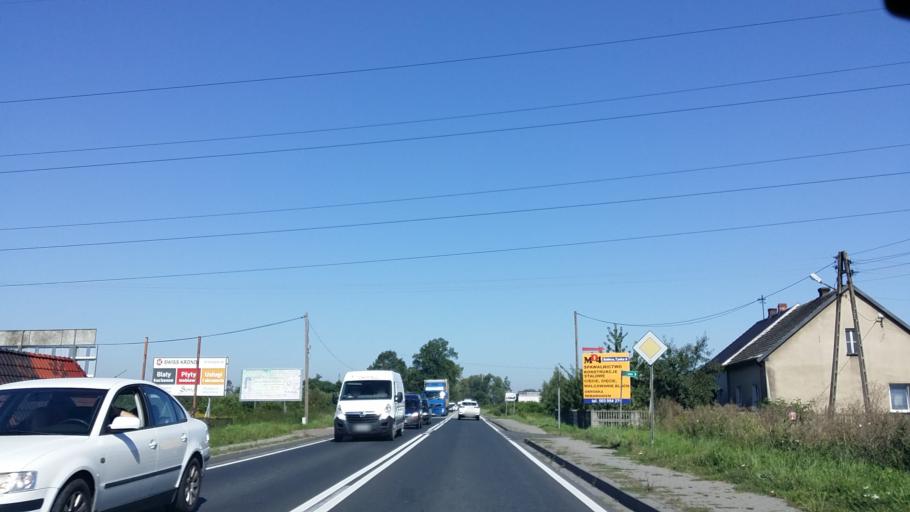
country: PL
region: Lesser Poland Voivodeship
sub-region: Powiat oswiecimski
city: Babice
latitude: 50.0578
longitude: 19.1975
